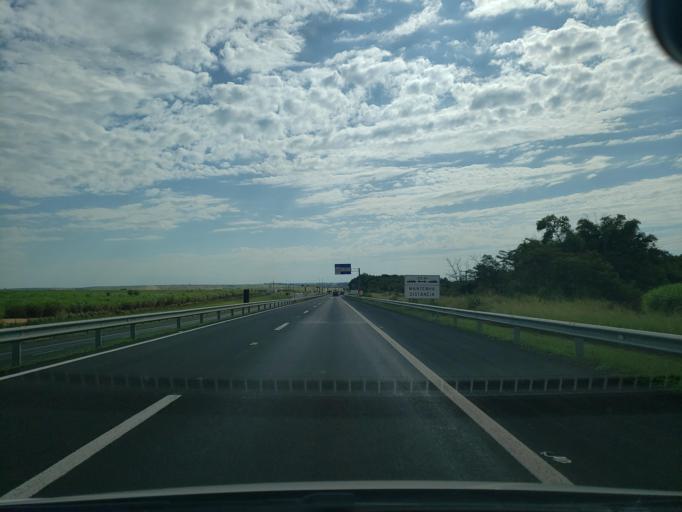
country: BR
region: Sao Paulo
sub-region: Promissao
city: Promissao
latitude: -21.6251
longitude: -49.8484
